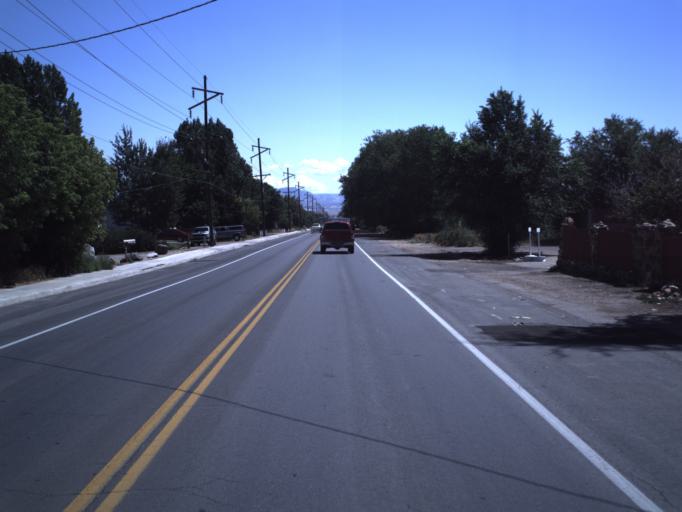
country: US
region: Utah
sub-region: Uintah County
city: Maeser
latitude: 40.4626
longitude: -109.5737
